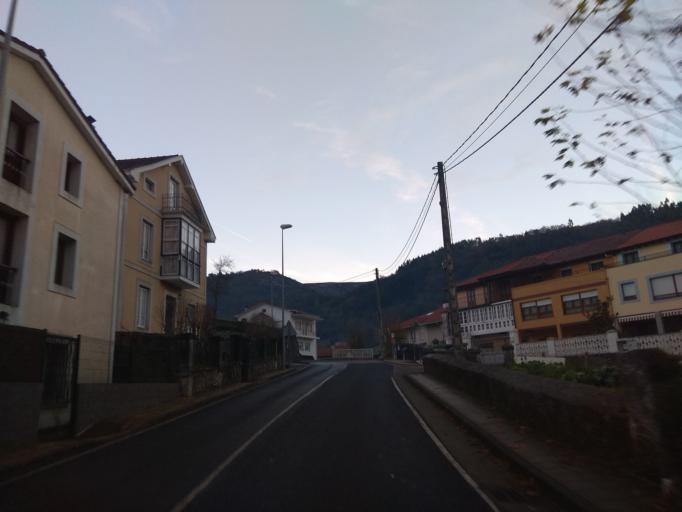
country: ES
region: Cantabria
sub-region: Provincia de Cantabria
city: Arredondo
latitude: 43.2736
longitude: -3.5985
